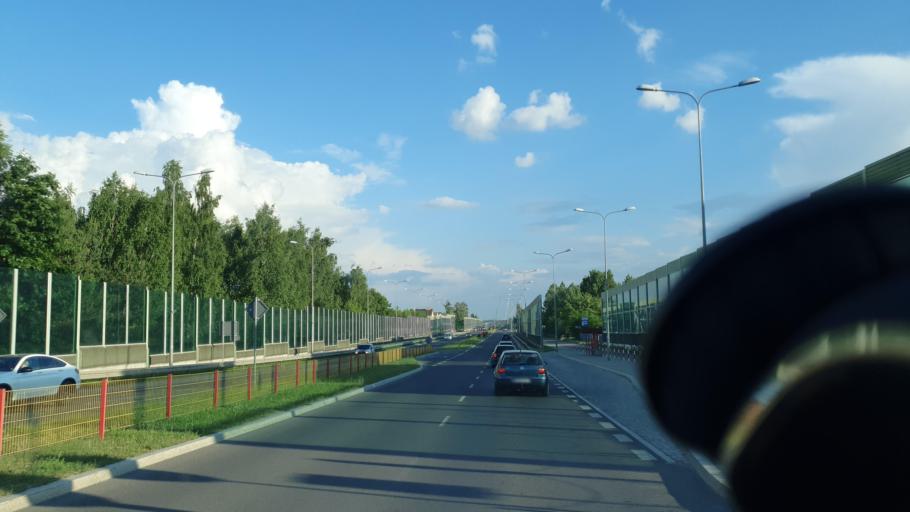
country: PL
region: Podlasie
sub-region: Bialystok
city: Bialystok
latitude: 53.1552
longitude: 23.2025
